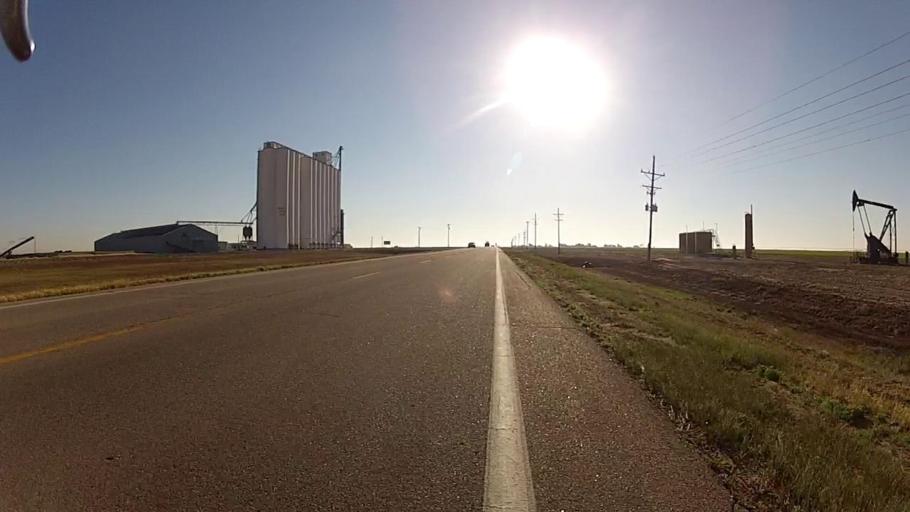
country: US
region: Kansas
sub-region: Haskell County
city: Sublette
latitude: 37.4871
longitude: -100.8297
